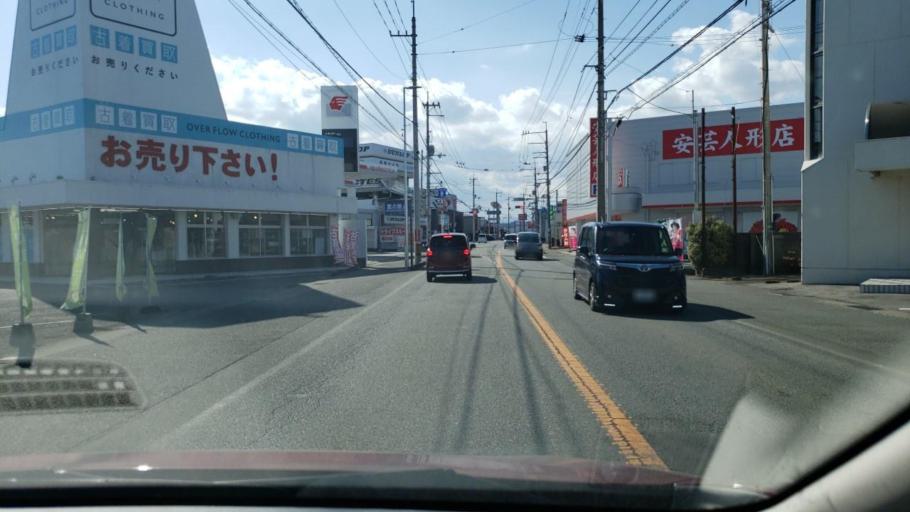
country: JP
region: Tokushima
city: Ishii
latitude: 34.1313
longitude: 134.4866
